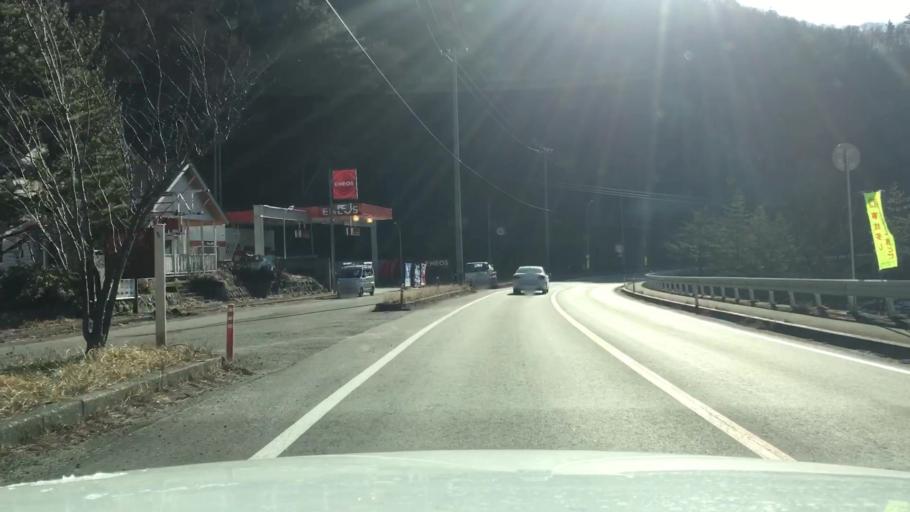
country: JP
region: Iwate
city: Tono
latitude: 39.6412
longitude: 141.5993
